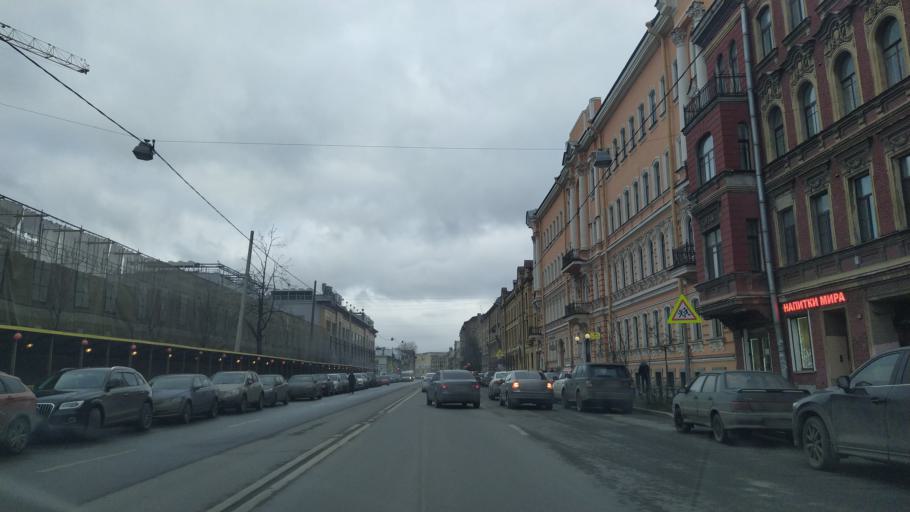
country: RU
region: St.-Petersburg
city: Centralniy
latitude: 59.9181
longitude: 30.3416
